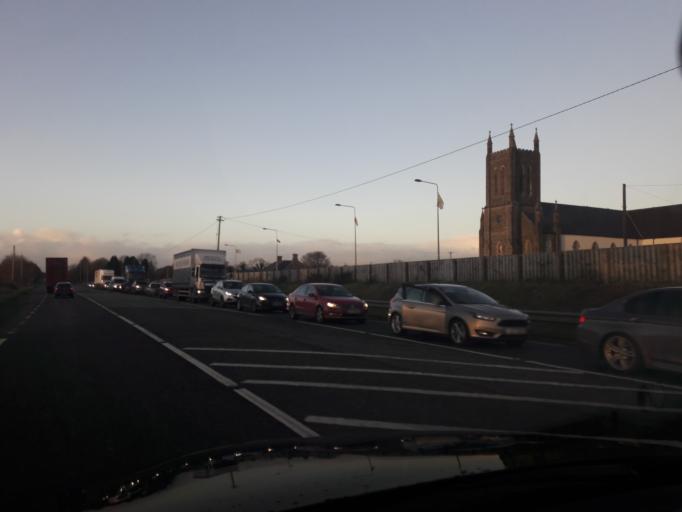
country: IE
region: Ulster
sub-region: County Monaghan
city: Monaghan
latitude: 54.2148
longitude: -6.8535
